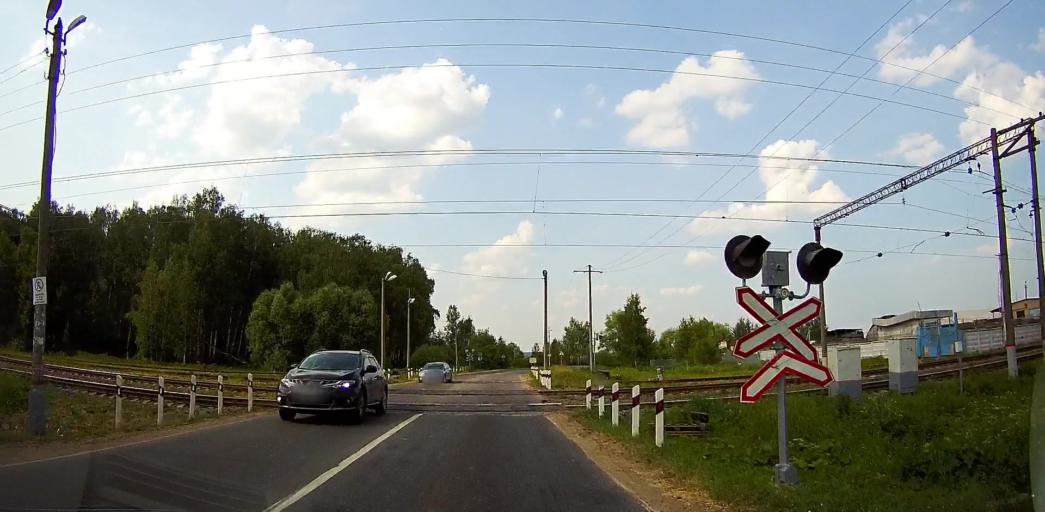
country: RU
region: Moskovskaya
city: Malino
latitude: 55.0555
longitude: 38.1416
